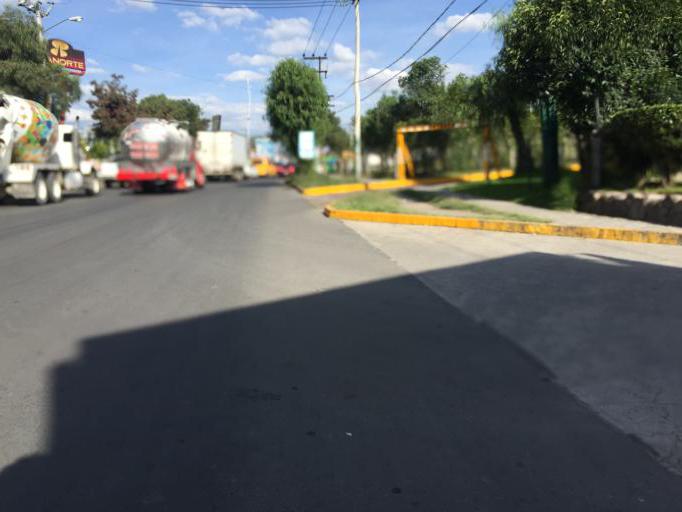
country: MX
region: Mexico
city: Cuautitlan
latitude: 19.6700
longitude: -99.2024
